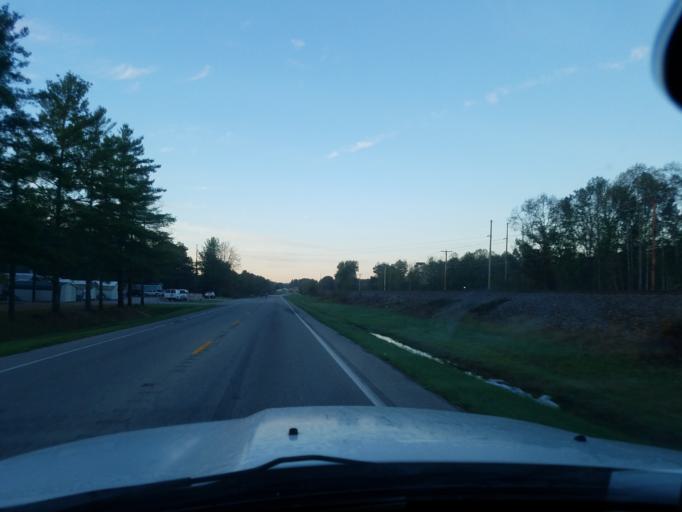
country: US
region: Kentucky
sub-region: Laurel County
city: North Corbin
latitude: 37.0394
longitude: -84.0571
